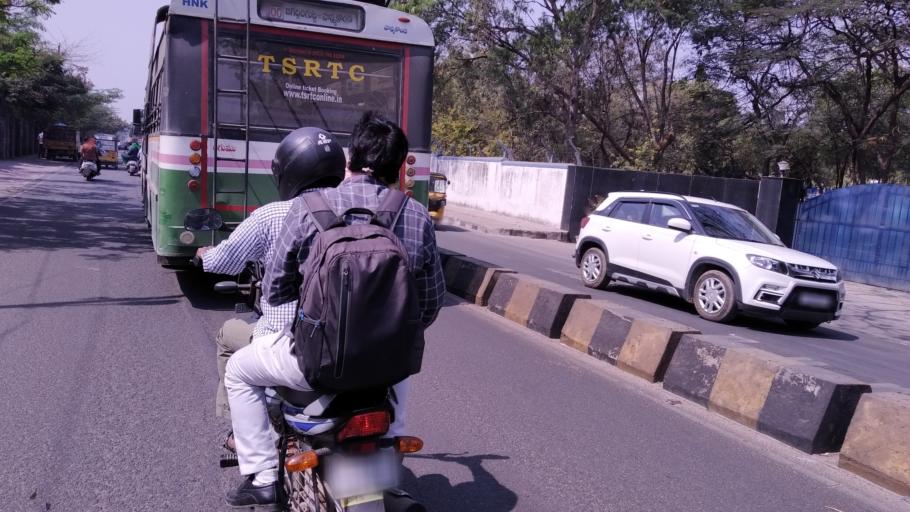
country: IN
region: Telangana
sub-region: Hyderabad
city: Malkajgiri
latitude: 17.4492
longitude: 78.4926
